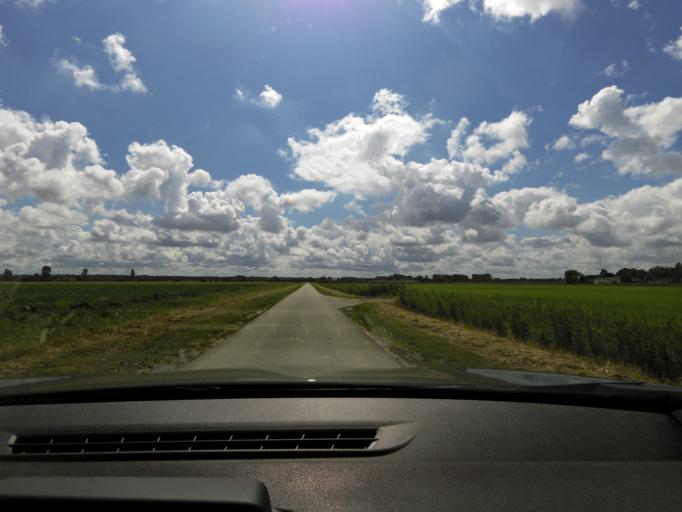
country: NL
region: South Holland
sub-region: Gemeente Hellevoetsluis
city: Nieuw-Helvoet
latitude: 51.8713
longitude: 4.0934
